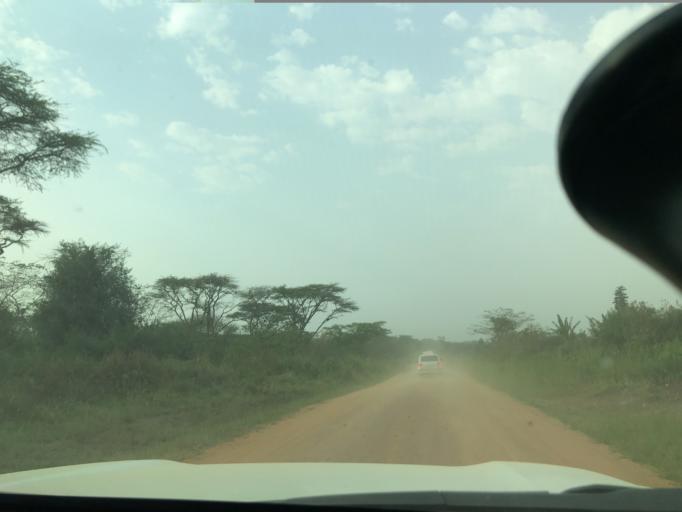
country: UG
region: Western Region
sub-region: Kasese District
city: Margherita
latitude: 0.2200
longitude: 29.6794
